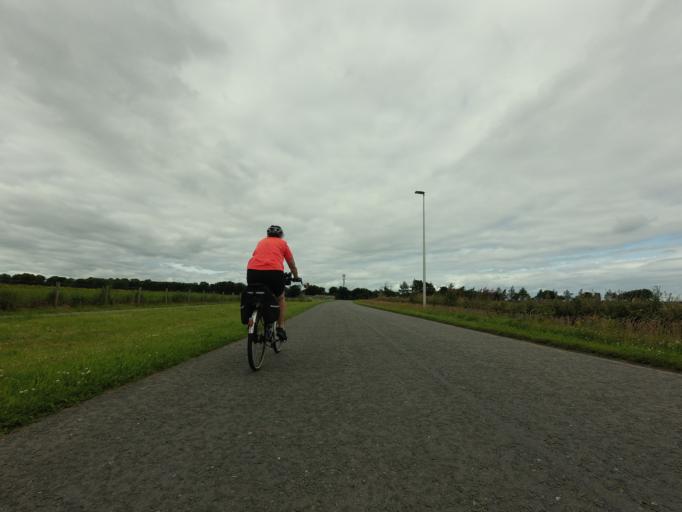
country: GB
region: Scotland
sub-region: Moray
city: Forres
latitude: 57.6138
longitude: -3.6254
